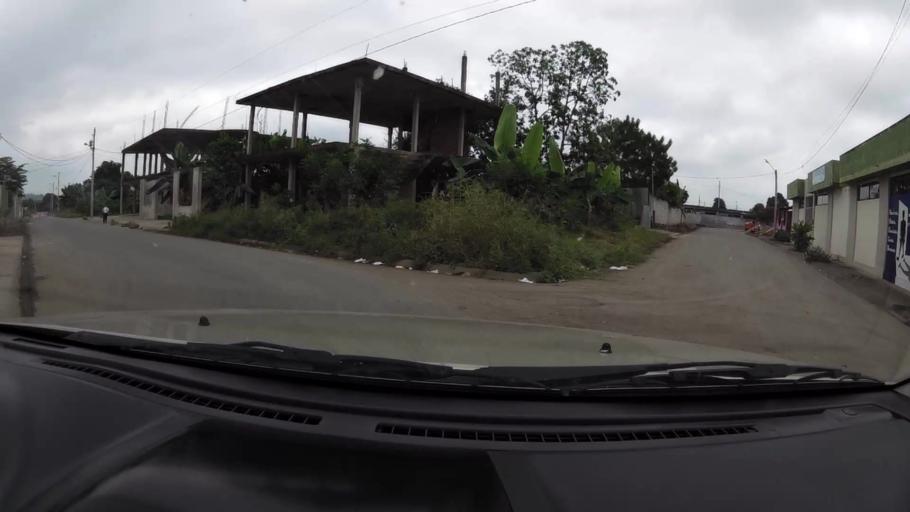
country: EC
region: El Oro
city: Pasaje
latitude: -3.2351
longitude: -79.8264
